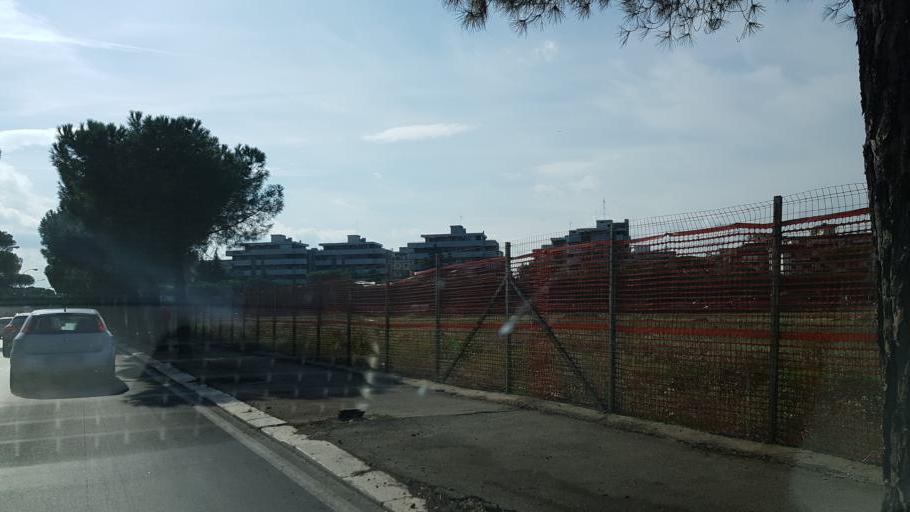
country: IT
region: Apulia
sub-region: Provincia di Foggia
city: Foggia
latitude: 41.4571
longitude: 15.5642
